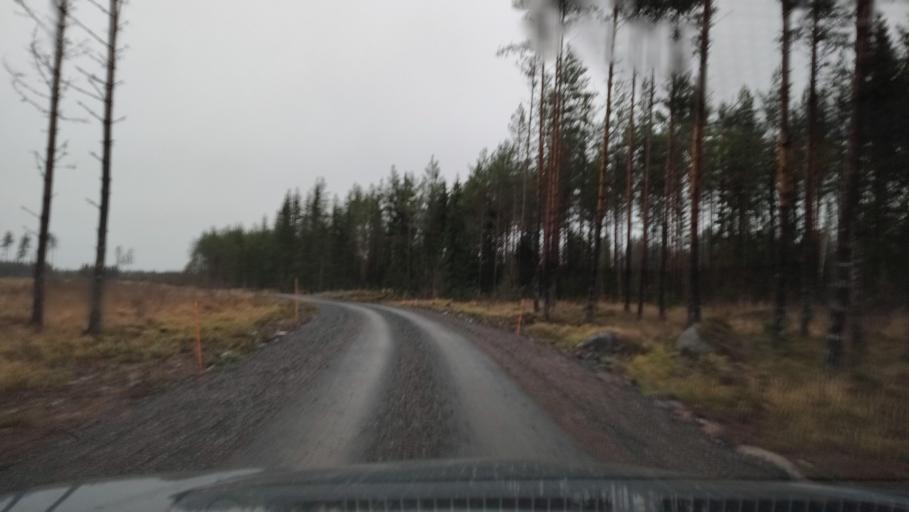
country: FI
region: Southern Ostrobothnia
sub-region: Suupohja
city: Karijoki
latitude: 62.1790
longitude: 21.6015
